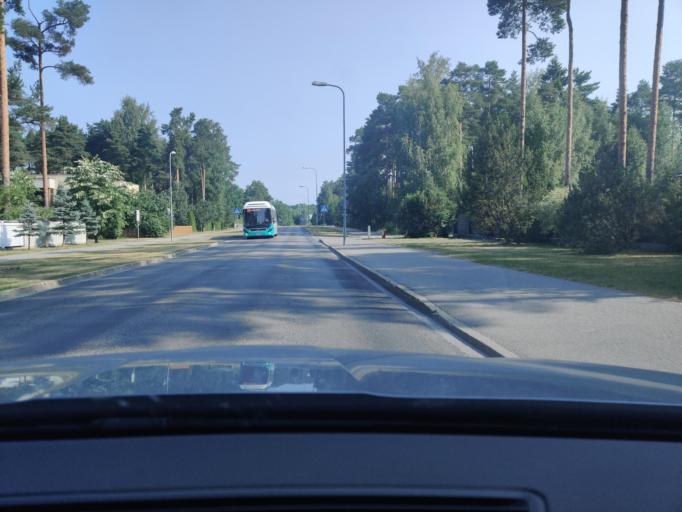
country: EE
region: Harju
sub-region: Saue vald
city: Laagri
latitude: 59.3577
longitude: 24.6116
